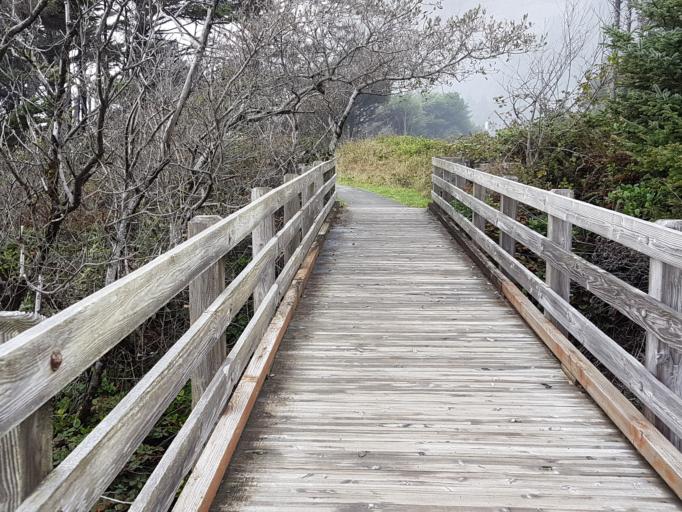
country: US
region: Oregon
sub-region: Lincoln County
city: Waldport
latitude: 44.2798
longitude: -124.1098
